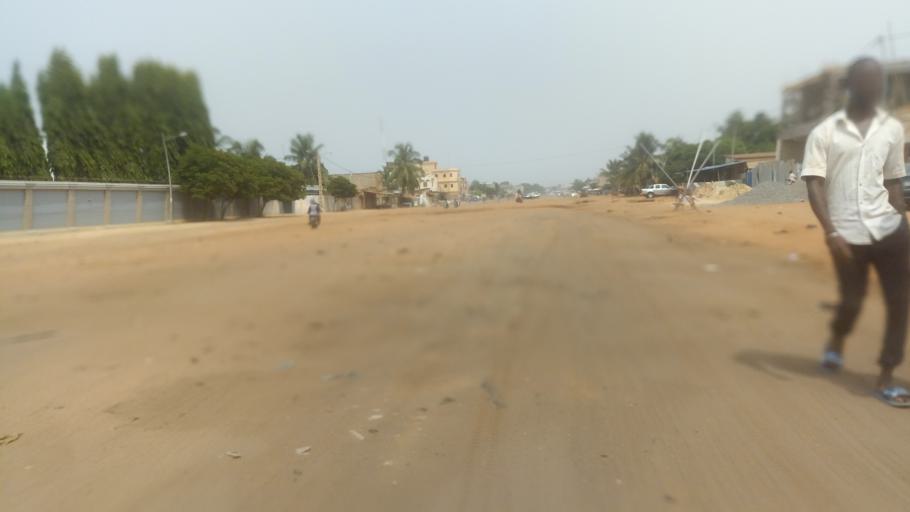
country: TG
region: Maritime
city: Lome
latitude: 6.1915
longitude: 1.1771
